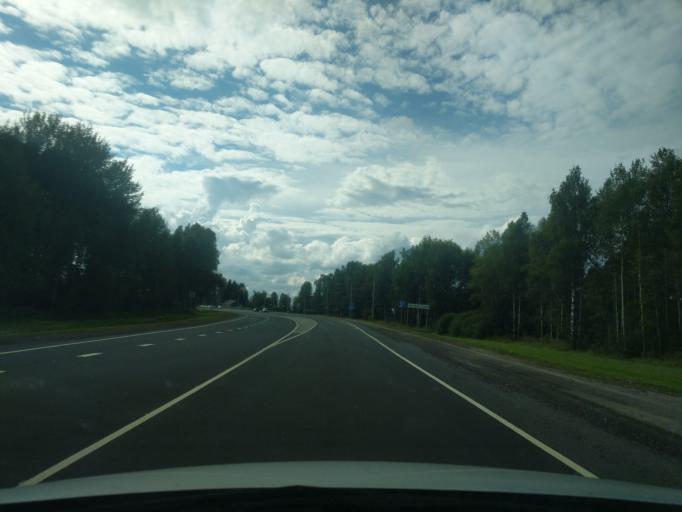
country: RU
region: Jaroslavl
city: Nekrasovskoye
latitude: 57.6371
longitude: 40.3937
